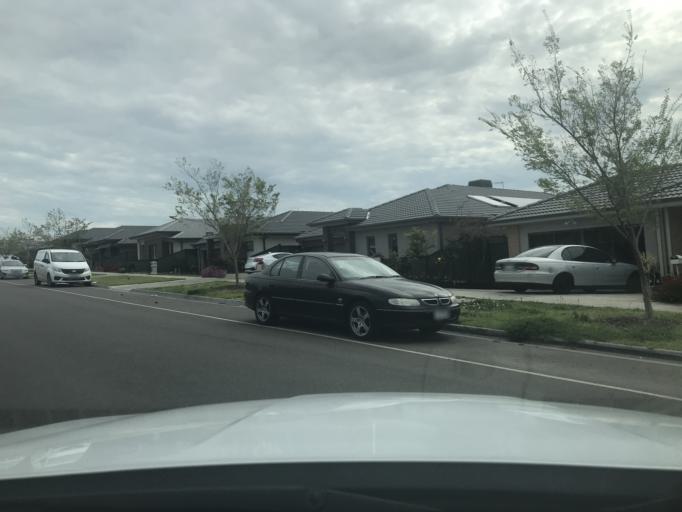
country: AU
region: Victoria
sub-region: Hume
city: Roxburgh Park
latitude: -37.5975
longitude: 144.8971
